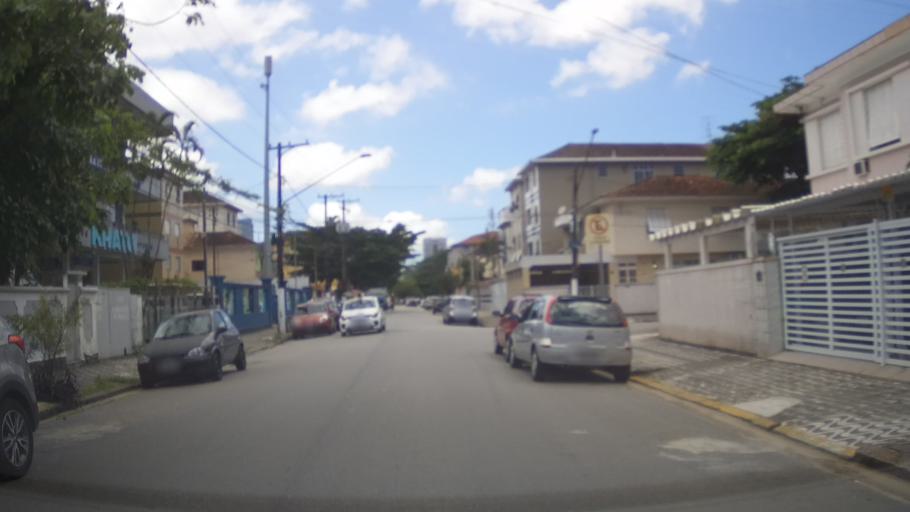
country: BR
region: Sao Paulo
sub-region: Santos
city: Santos
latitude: -23.9480
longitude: -46.3403
